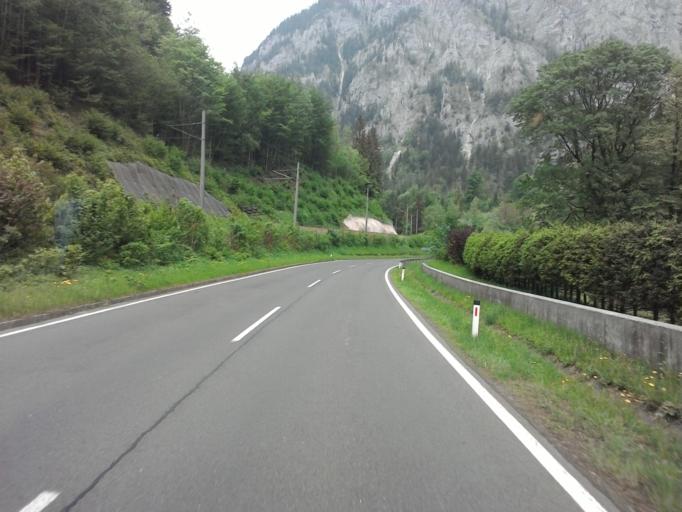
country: AT
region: Styria
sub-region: Politischer Bezirk Leoben
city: Eisenerz
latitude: 47.5700
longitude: 14.8496
